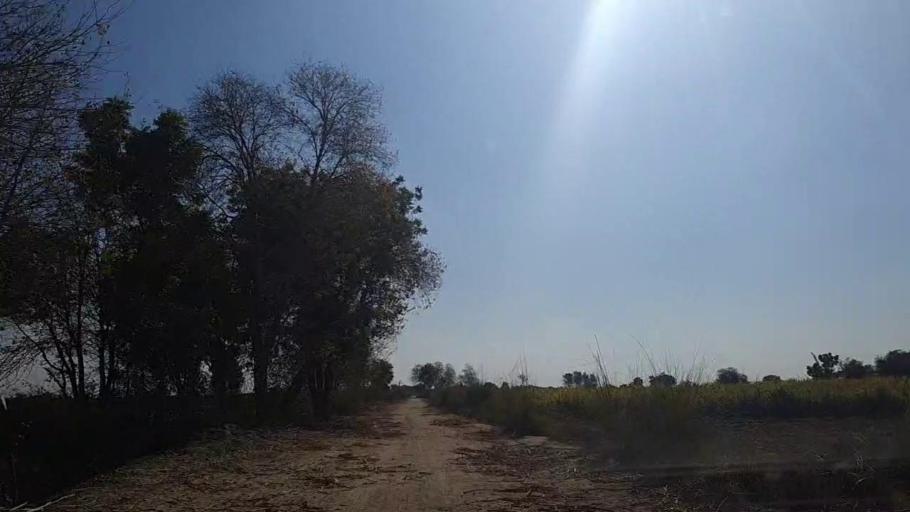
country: PK
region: Sindh
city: Sakrand
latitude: 26.2410
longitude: 68.1998
